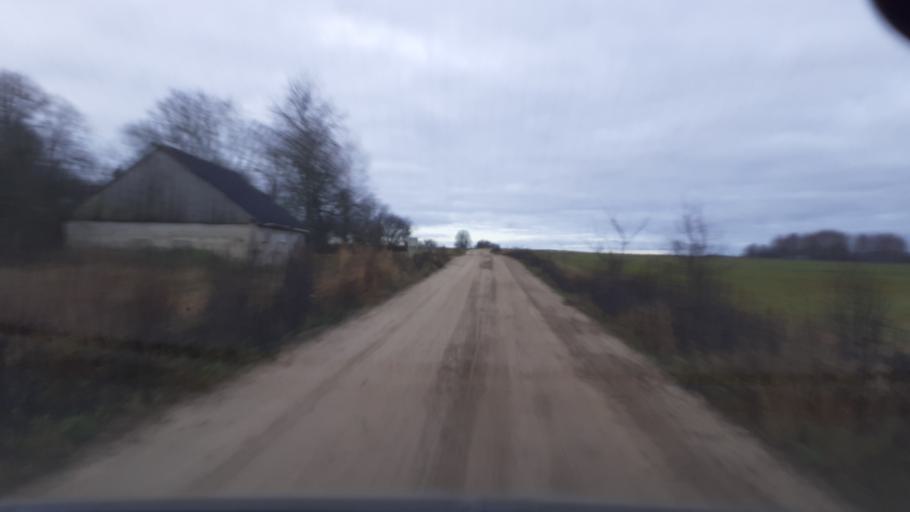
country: LV
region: Kuldigas Rajons
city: Kuldiga
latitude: 56.9977
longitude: 21.9094
